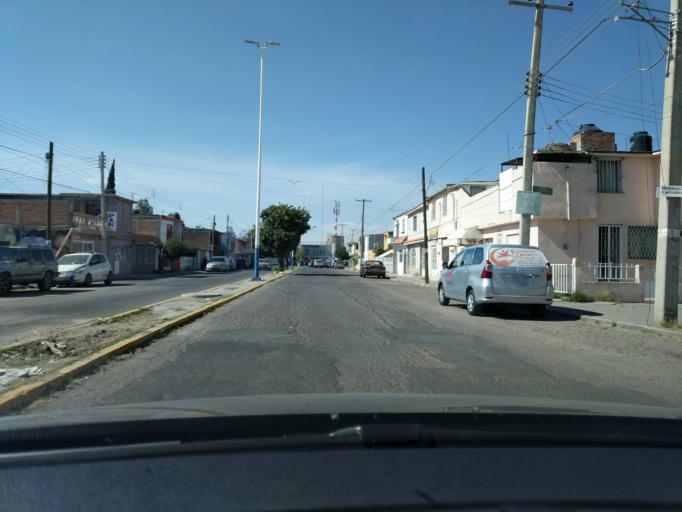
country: MX
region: Durango
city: Victoria de Durango
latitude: 24.0069
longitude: -104.6547
